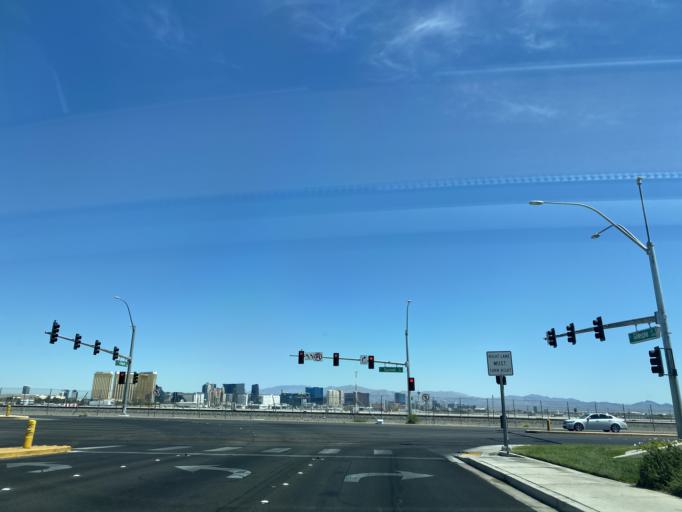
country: US
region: Nevada
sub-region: Clark County
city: Paradise
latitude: 36.0708
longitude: -115.1635
